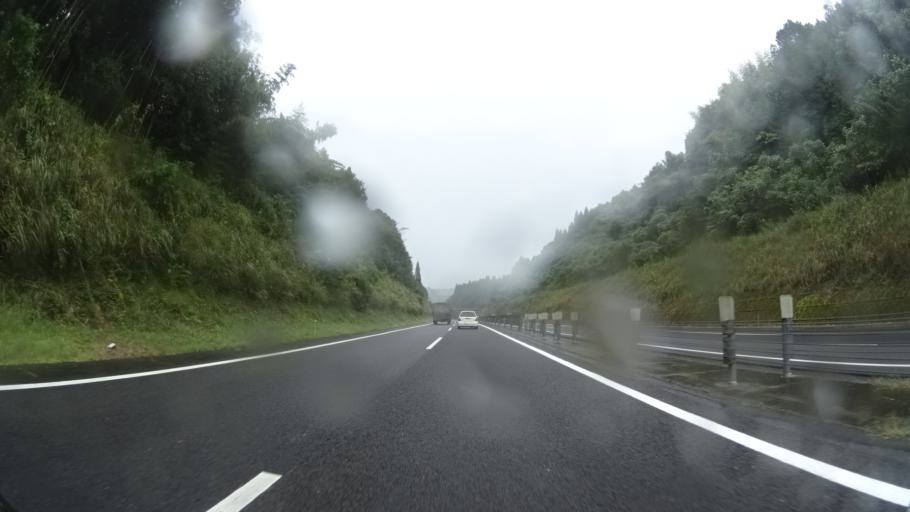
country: JP
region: Kagoshima
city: Okuchi-shinohara
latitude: 31.9869
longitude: 130.7544
